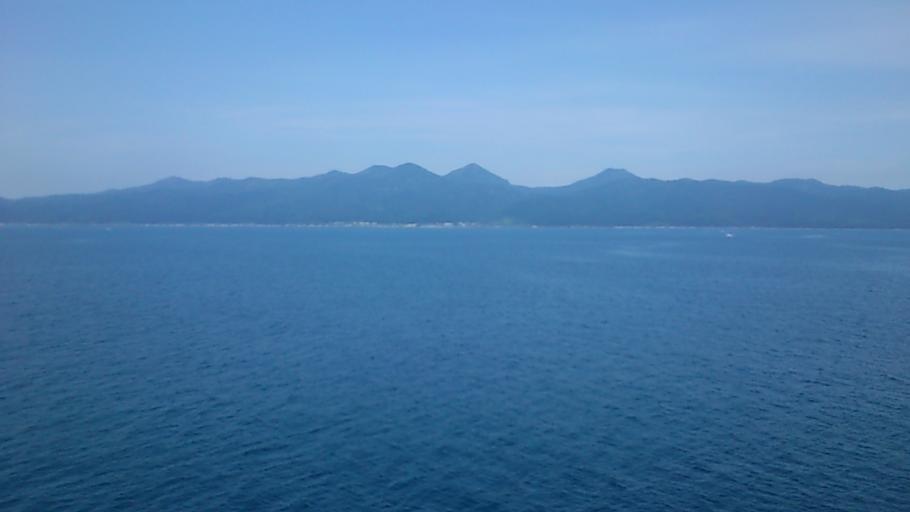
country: JP
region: Aomori
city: Aomori Shi
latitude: 41.1465
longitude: 140.7063
